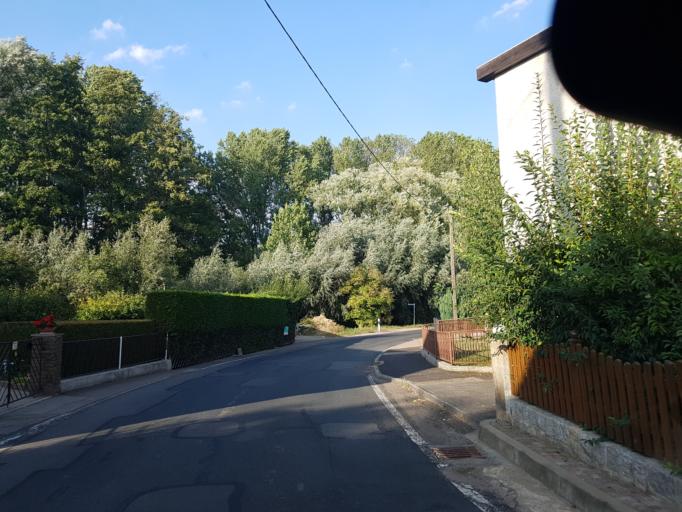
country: DE
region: Saxony
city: Ostrau
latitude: 51.1930
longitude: 13.1399
